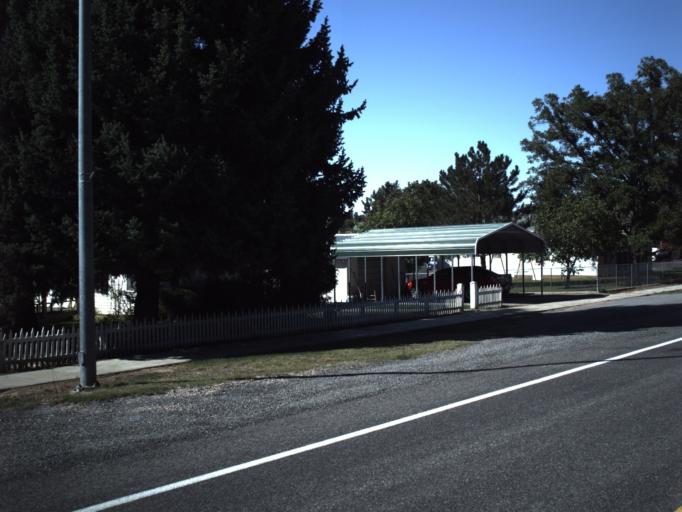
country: US
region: Utah
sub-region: Millard County
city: Fillmore
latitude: 39.0968
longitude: -112.2709
